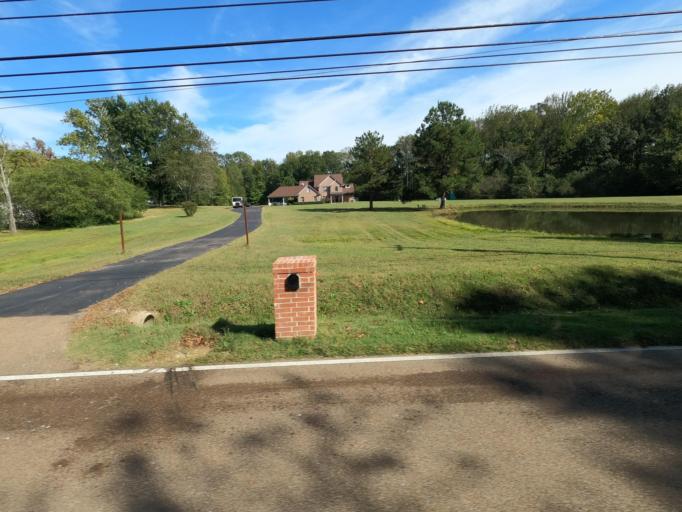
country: US
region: Tennessee
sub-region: Fayette County
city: Hickory Withe
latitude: 35.2338
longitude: -89.6500
